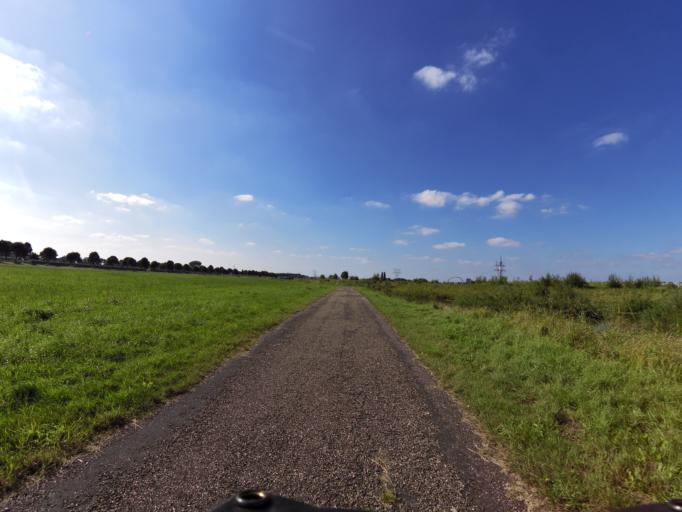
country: NL
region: South Holland
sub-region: Gemeente Binnenmaas
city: Heinenoord
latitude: 51.8572
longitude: 4.4609
